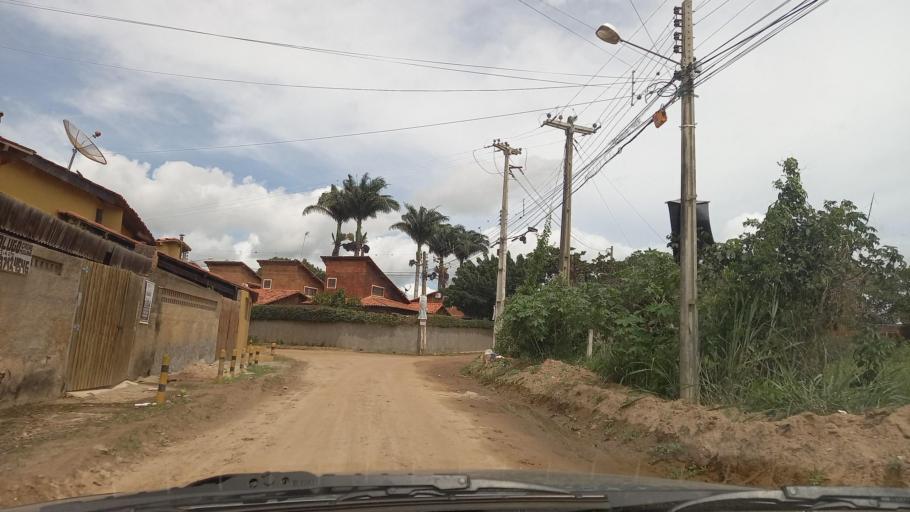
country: BR
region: Pernambuco
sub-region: Gravata
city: Gravata
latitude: -8.1954
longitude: -35.5892
